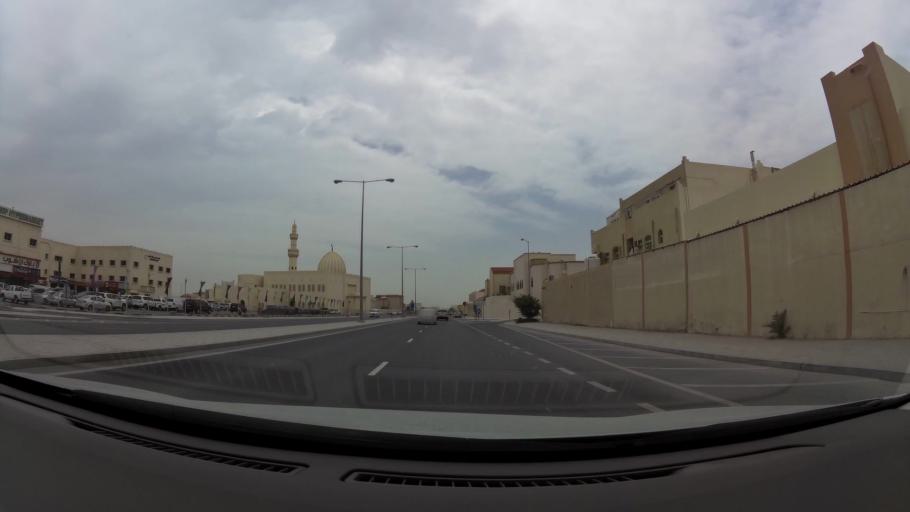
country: QA
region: Baladiyat ar Rayyan
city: Ar Rayyan
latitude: 25.2407
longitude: 51.4659
